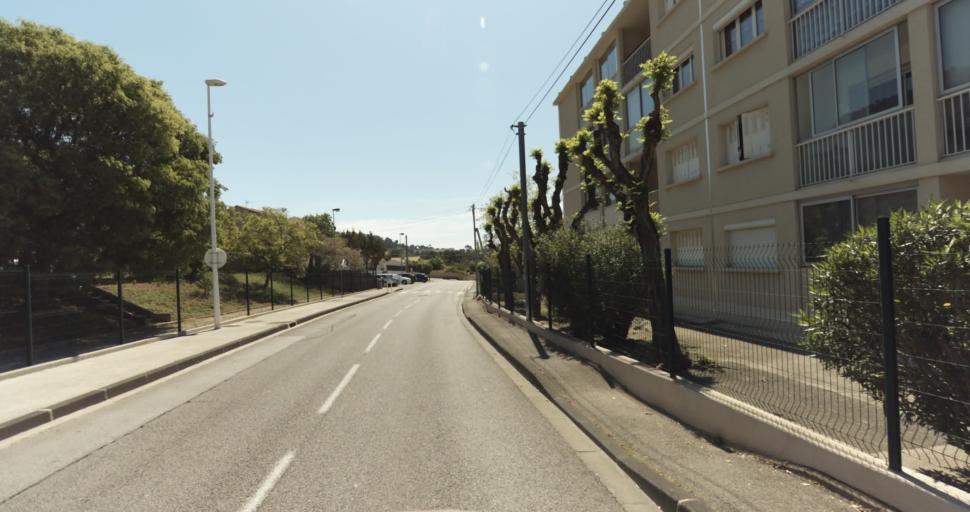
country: FR
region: Provence-Alpes-Cote d'Azur
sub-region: Departement du Var
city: Le Revest-les-Eaux
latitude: 43.1445
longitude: 5.9056
